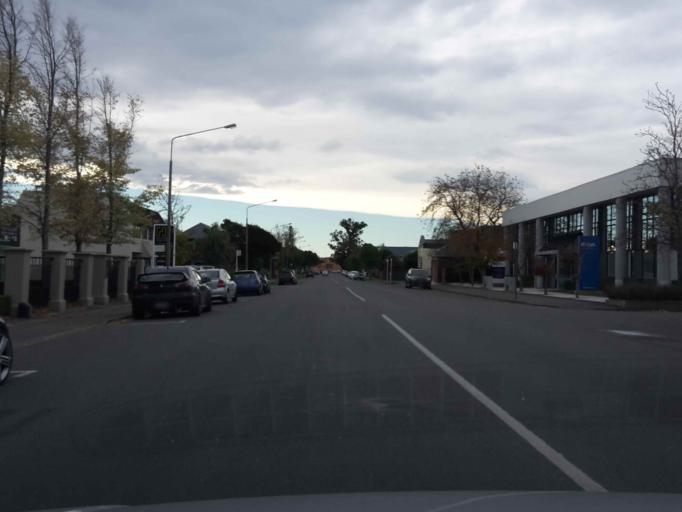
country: NZ
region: Canterbury
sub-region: Christchurch City
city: Christchurch
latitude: -43.5333
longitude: 172.6066
